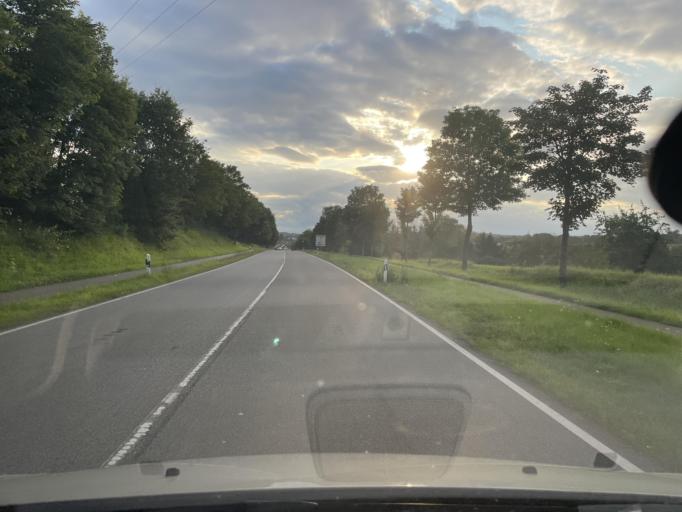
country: DE
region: Saarland
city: Sankt Ingbert
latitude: 49.2863
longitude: 7.1410
